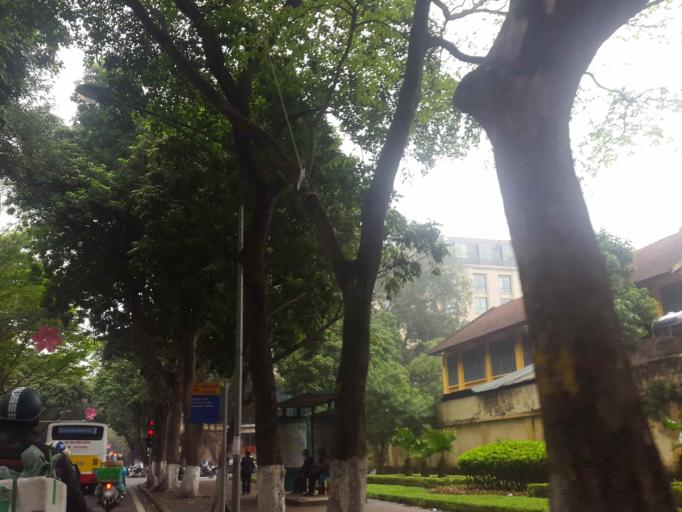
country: VN
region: Ha Noi
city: Hoan Kiem
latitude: 21.0407
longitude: 105.8413
